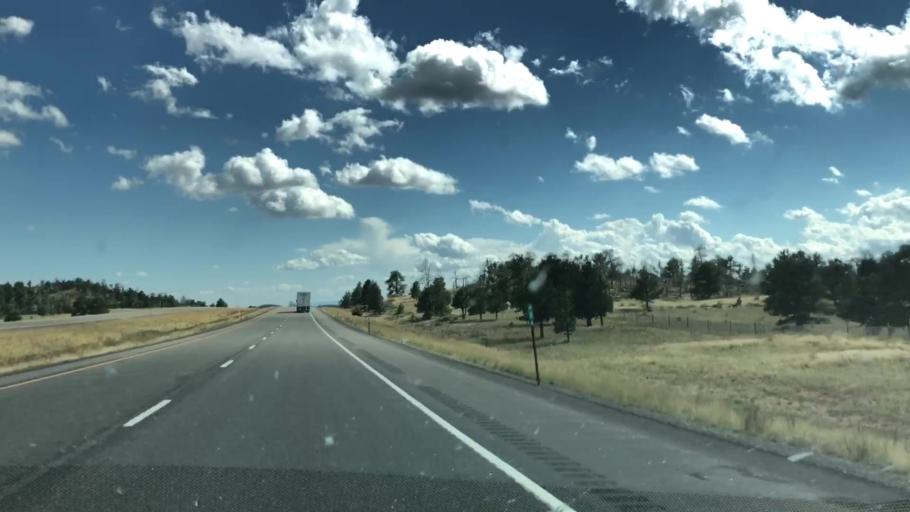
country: US
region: Wyoming
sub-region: Albany County
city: Laramie
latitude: 41.0165
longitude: -105.4207
